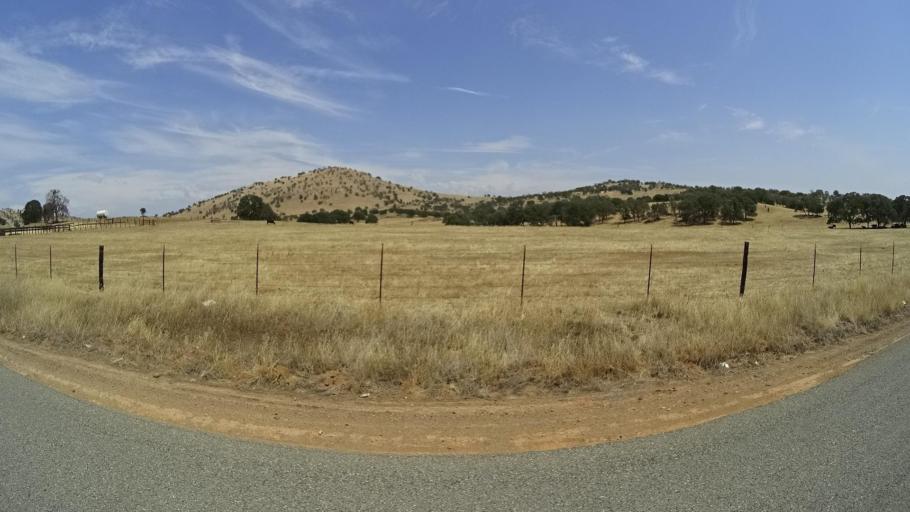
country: US
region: California
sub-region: Merced County
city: Planada
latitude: 37.6072
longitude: -120.3082
